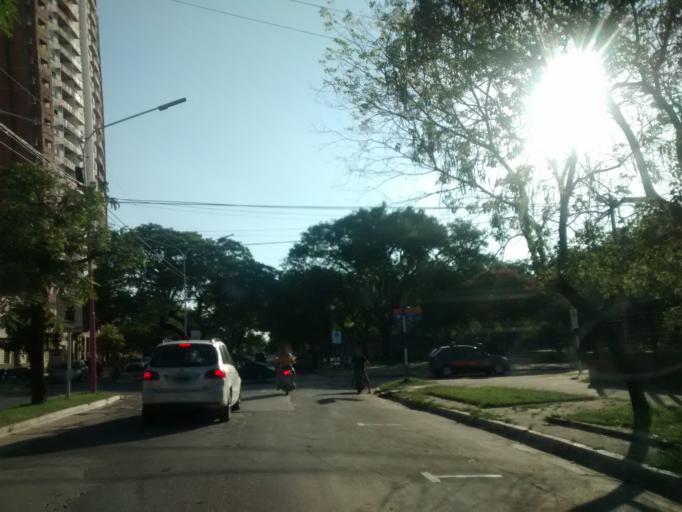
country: AR
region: Chaco
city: Resistencia
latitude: -27.4578
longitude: -58.9854
